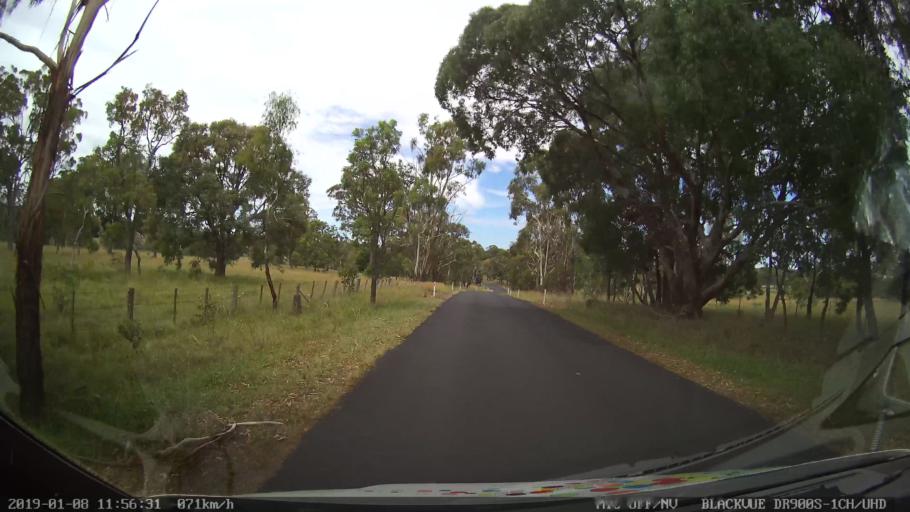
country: AU
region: New South Wales
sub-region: Armidale Dumaresq
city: Armidale
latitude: -30.4409
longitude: 151.5650
